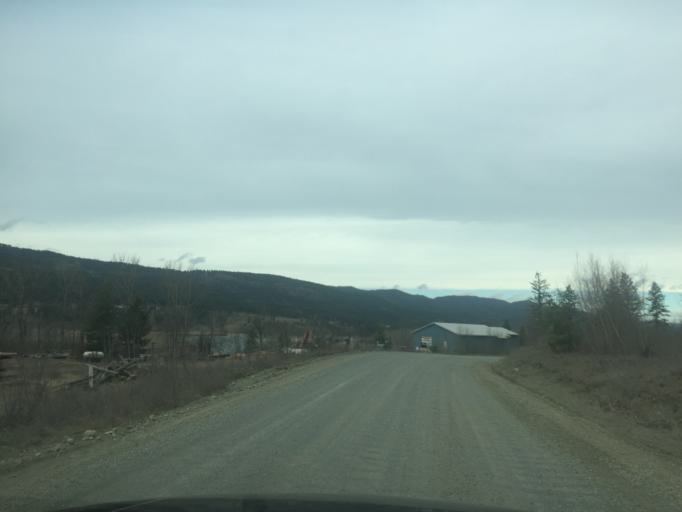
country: CA
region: British Columbia
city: Kamloops
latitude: 51.2735
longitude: -120.1529
